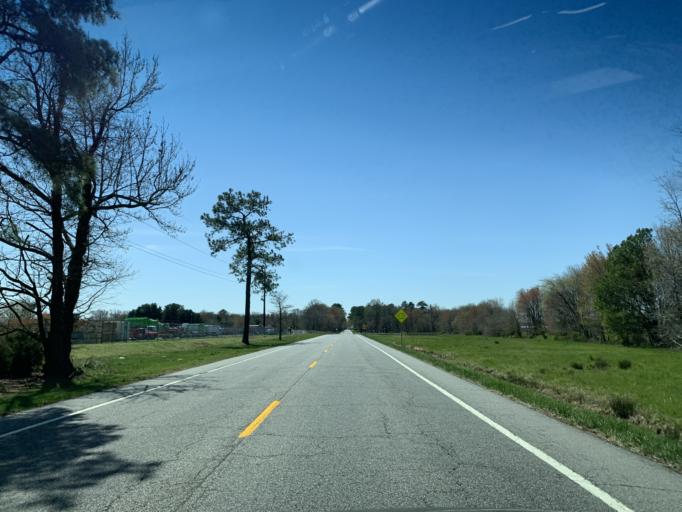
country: US
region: Maryland
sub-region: Talbot County
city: Easton
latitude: 38.8426
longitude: -76.0235
